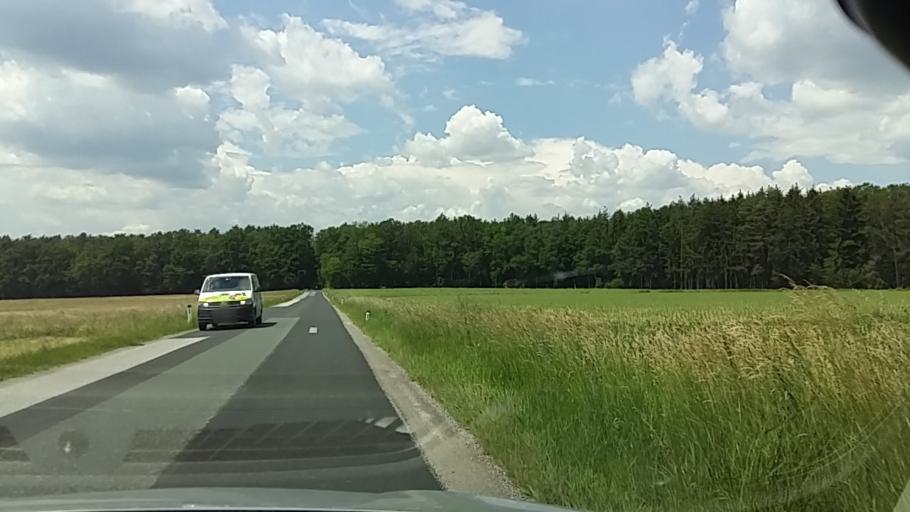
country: AT
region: Styria
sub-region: Politischer Bezirk Hartberg-Fuerstenfeld
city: Bad Blumau
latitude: 47.1208
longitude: 16.0362
